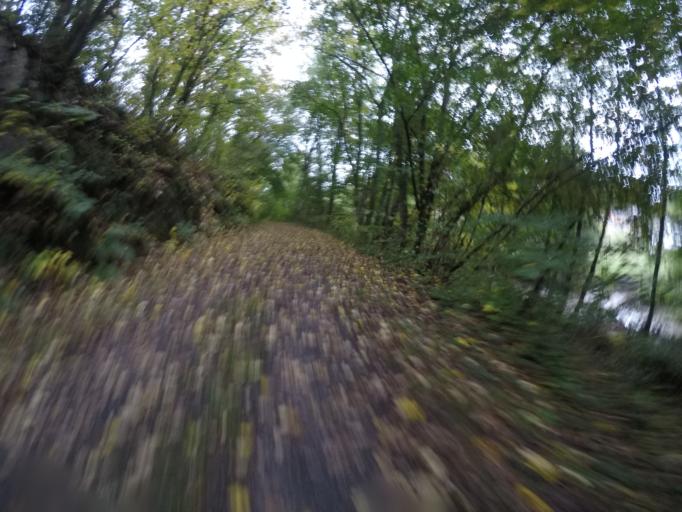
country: BE
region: Wallonia
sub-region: Province du Luxembourg
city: Fauvillers
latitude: 49.8516
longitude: 5.6978
